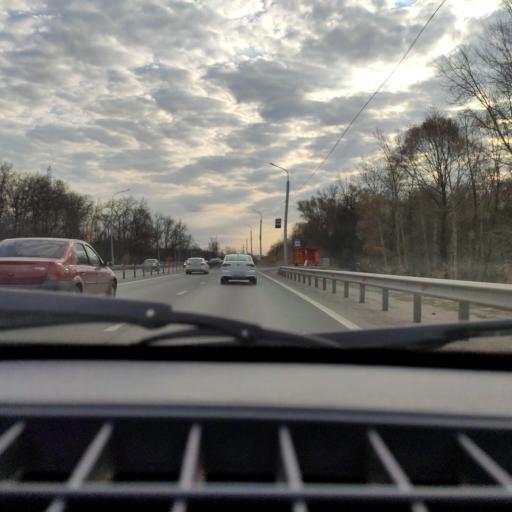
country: RU
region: Bashkortostan
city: Ufa
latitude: 54.6995
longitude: 55.8763
